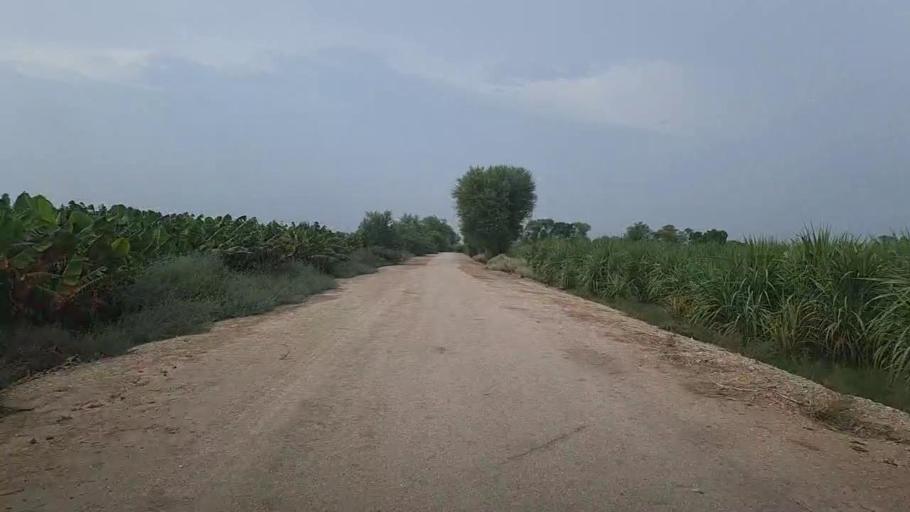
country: PK
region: Sindh
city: Karaundi
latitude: 26.9815
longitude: 68.4339
